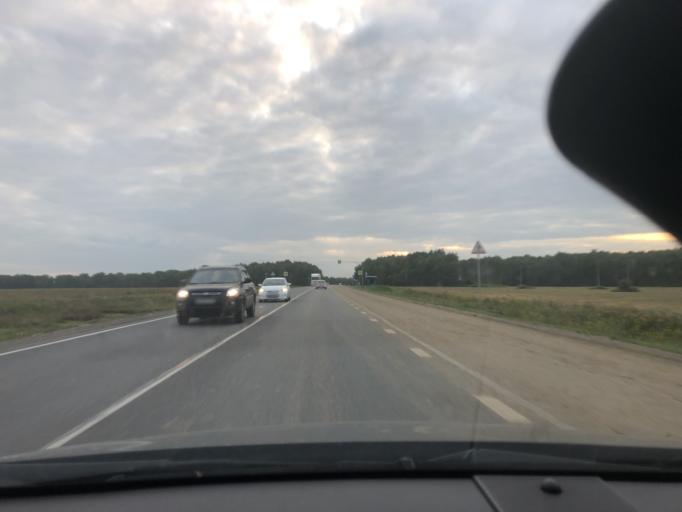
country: RU
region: Tula
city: Khanino
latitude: 54.3714
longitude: 36.6731
